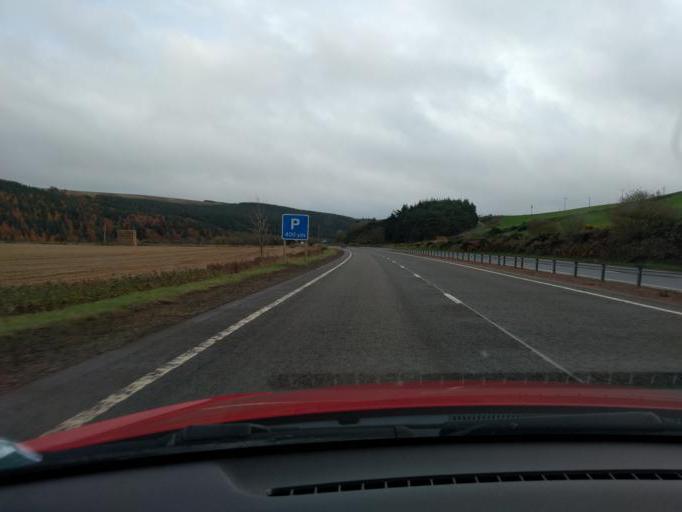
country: GB
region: Scotland
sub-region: The Scottish Borders
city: Duns
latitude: 55.9079
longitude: -2.3341
